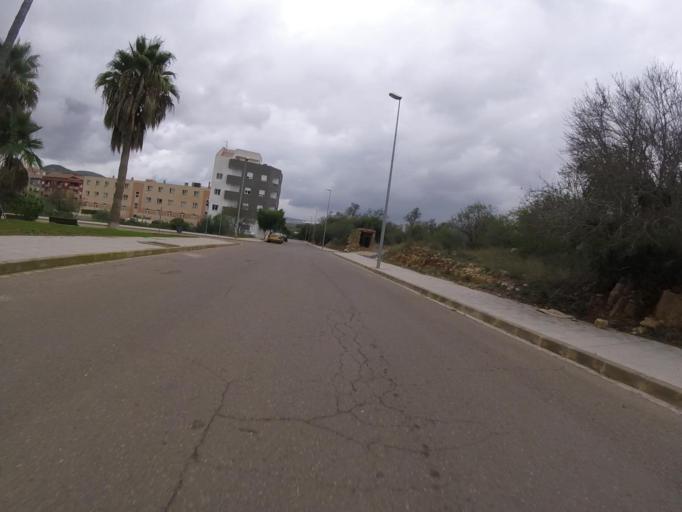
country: ES
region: Valencia
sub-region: Provincia de Castello
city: Cabanes
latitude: 40.1586
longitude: 0.0454
